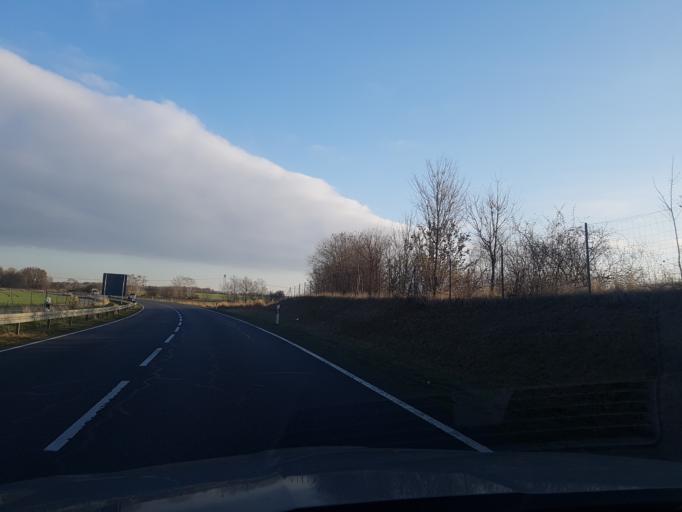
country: DE
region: Brandenburg
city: Luckau
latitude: 51.8436
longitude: 13.6792
